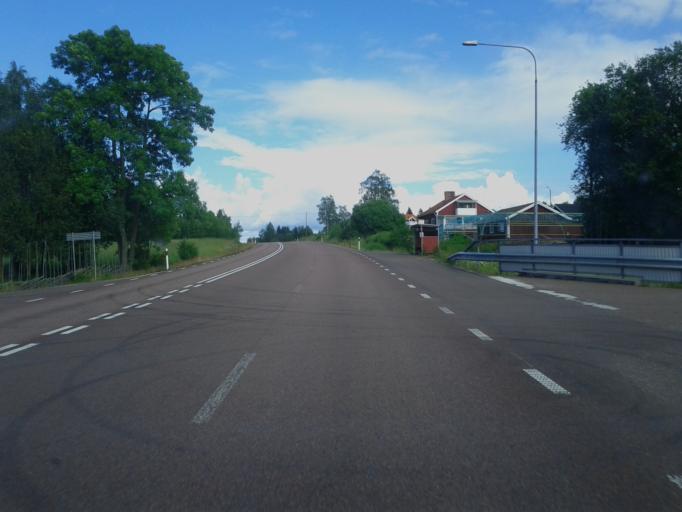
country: SE
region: Dalarna
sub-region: Rattviks Kommun
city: Raettvik
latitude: 60.8432
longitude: 15.1260
